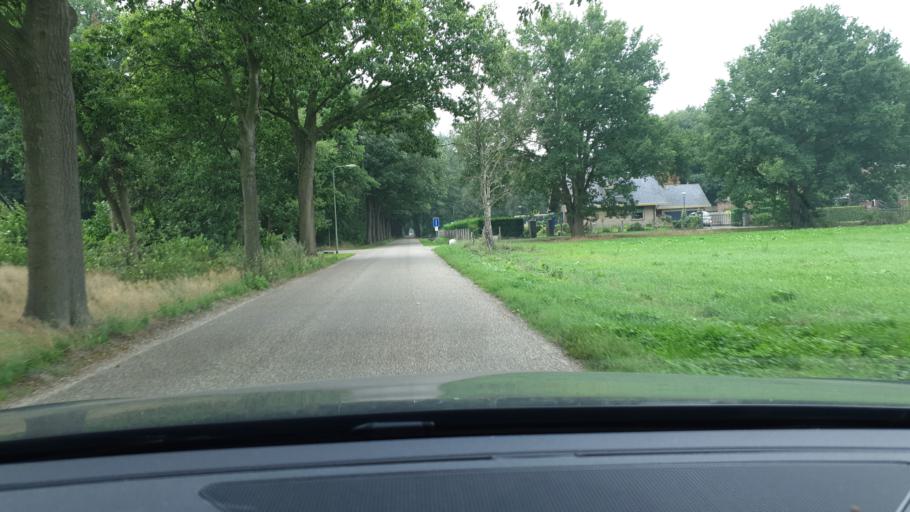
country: NL
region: North Brabant
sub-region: Gemeente Oss
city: Berghem
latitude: 51.7556
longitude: 5.5679
